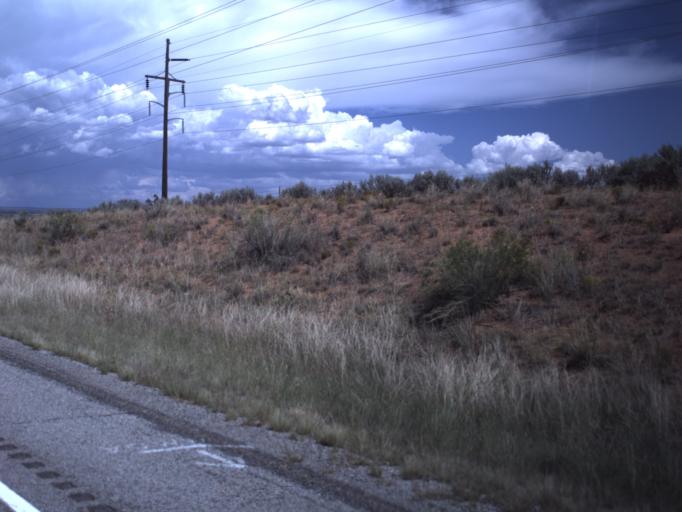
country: US
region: Utah
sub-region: San Juan County
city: Blanding
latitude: 37.5277
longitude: -109.4941
